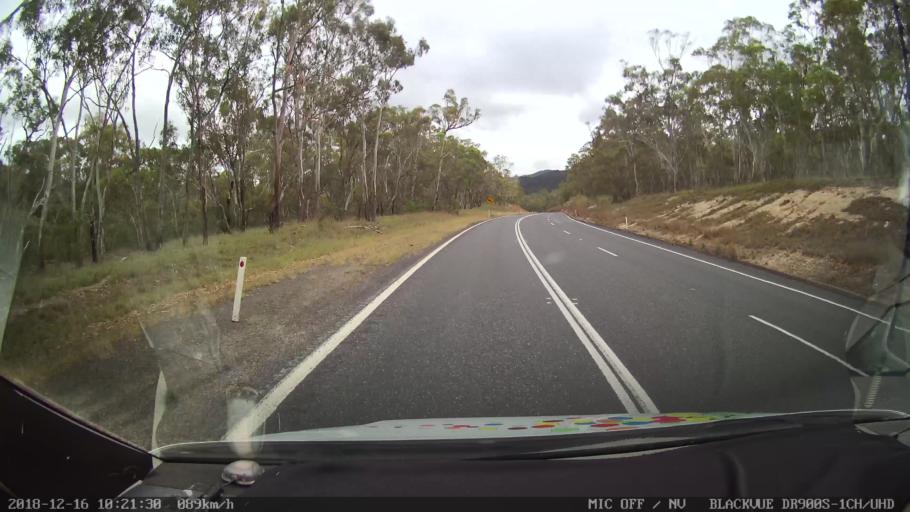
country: AU
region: New South Wales
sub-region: Tenterfield Municipality
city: Carrolls Creek
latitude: -29.2059
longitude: 152.0127
